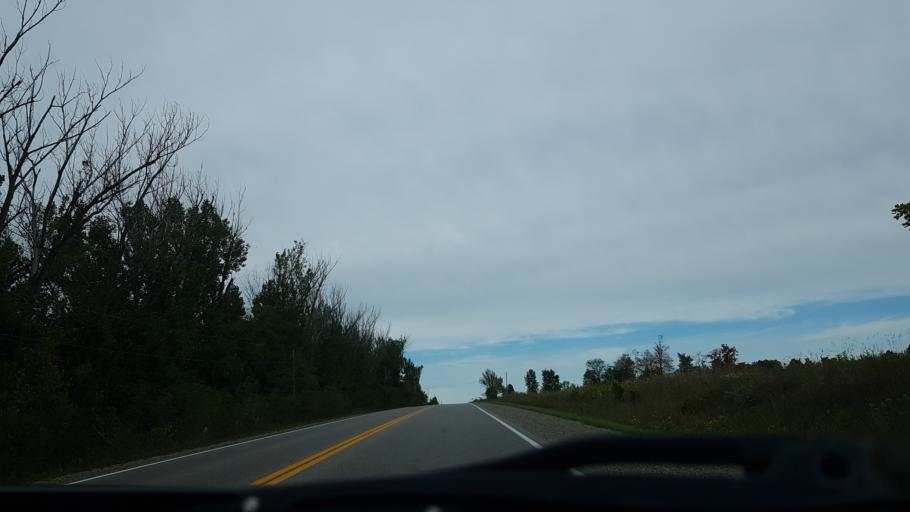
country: CA
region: Ontario
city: Shelburne
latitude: 44.0957
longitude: -80.0223
